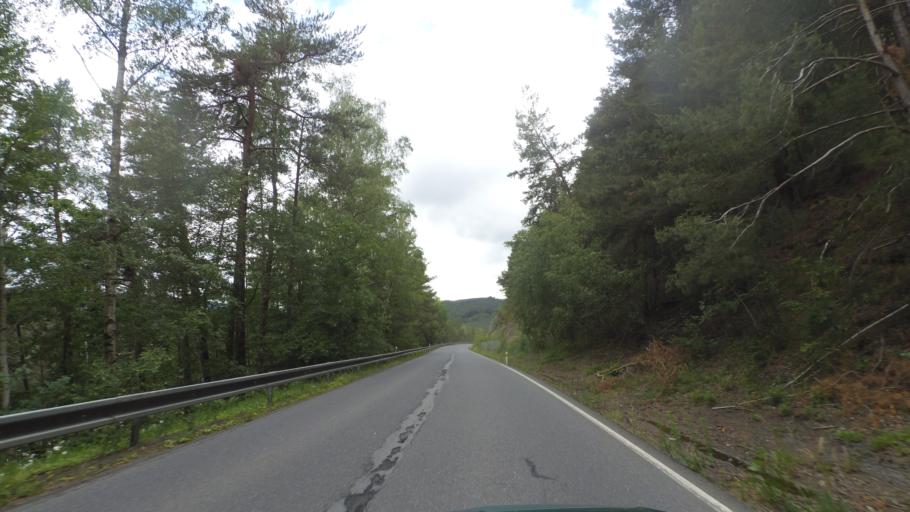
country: CZ
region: Plzensky
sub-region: Okres Klatovy
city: Nyrsko
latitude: 49.2592
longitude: 13.1522
